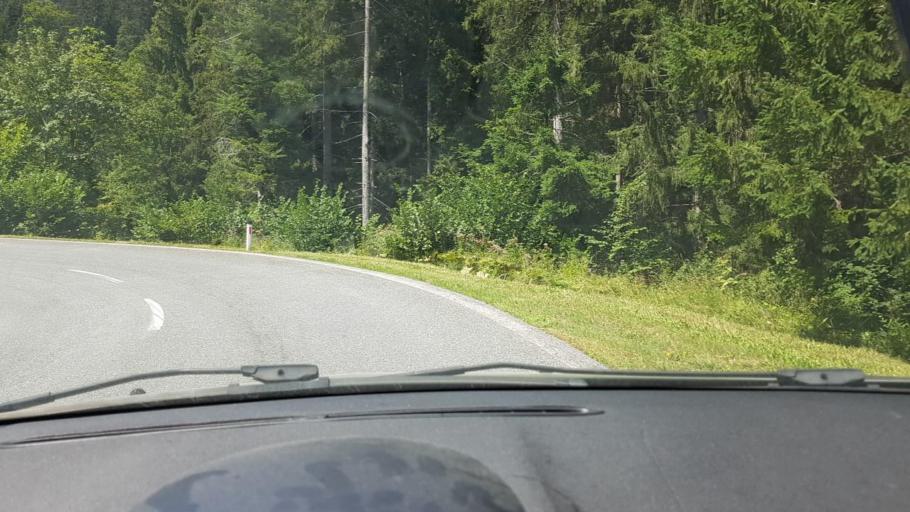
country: SI
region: Jezersko
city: Zgornje Jezersko
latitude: 46.4223
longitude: 14.5437
